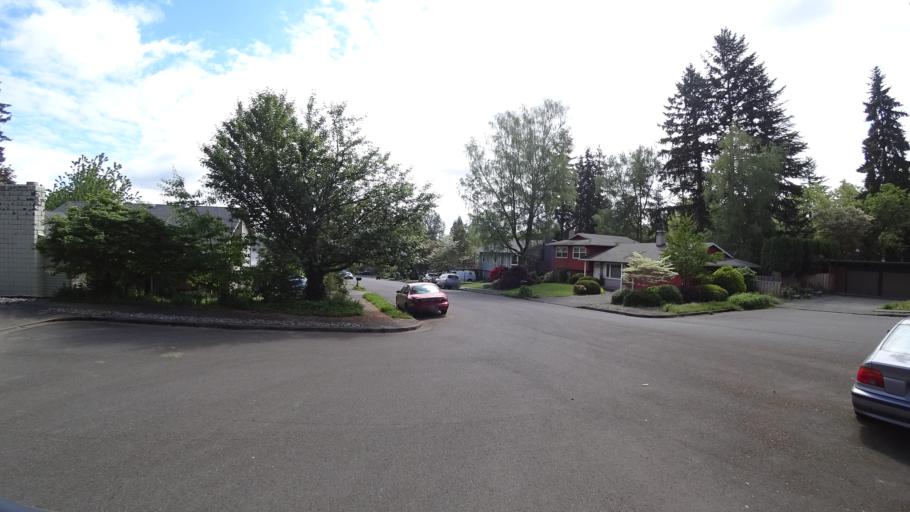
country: US
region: Oregon
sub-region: Washington County
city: Beaverton
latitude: 45.4675
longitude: -122.8126
